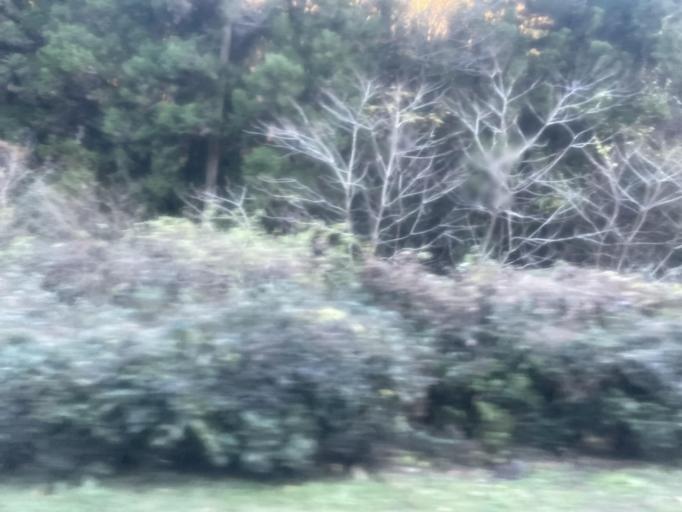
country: JP
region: Saitama
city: Yorii
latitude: 36.0869
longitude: 139.1730
